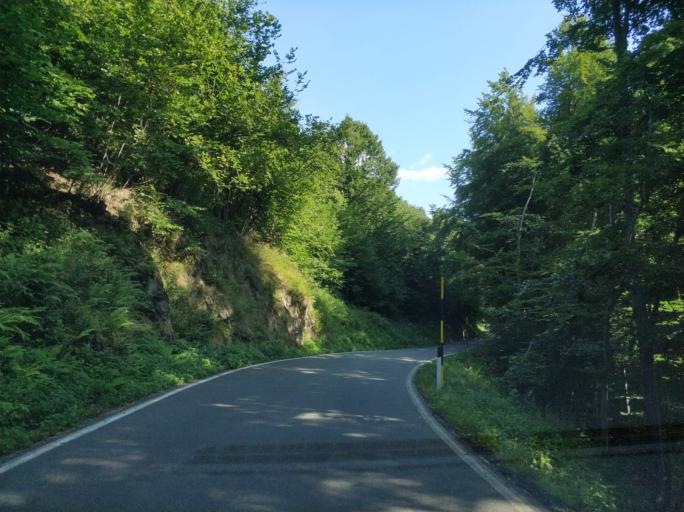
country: IT
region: Piedmont
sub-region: Provincia di Torino
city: Rubiana
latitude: 45.1828
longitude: 7.3709
